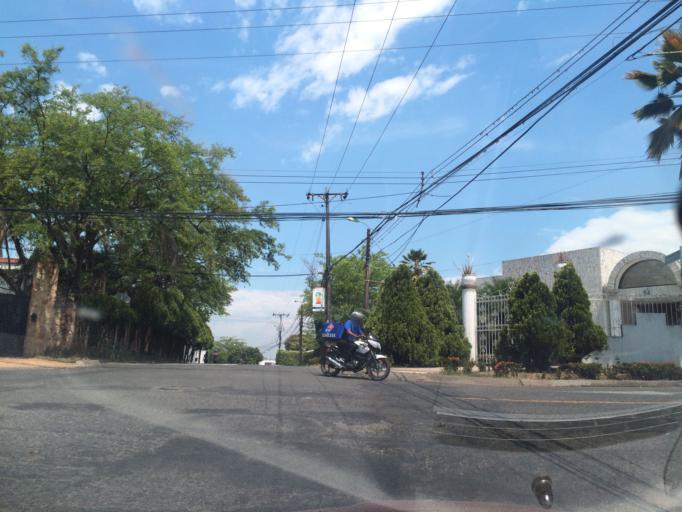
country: CO
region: Valle del Cauca
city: Cali
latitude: 3.3597
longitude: -76.5382
